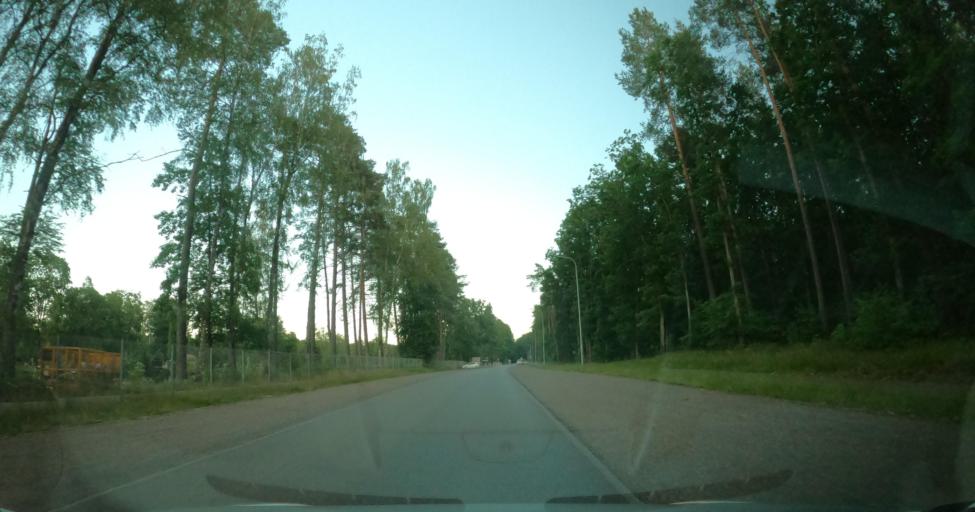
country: PL
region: Pomeranian Voivodeship
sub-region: Powiat leborski
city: Lebork
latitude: 54.5247
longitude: 17.7763
